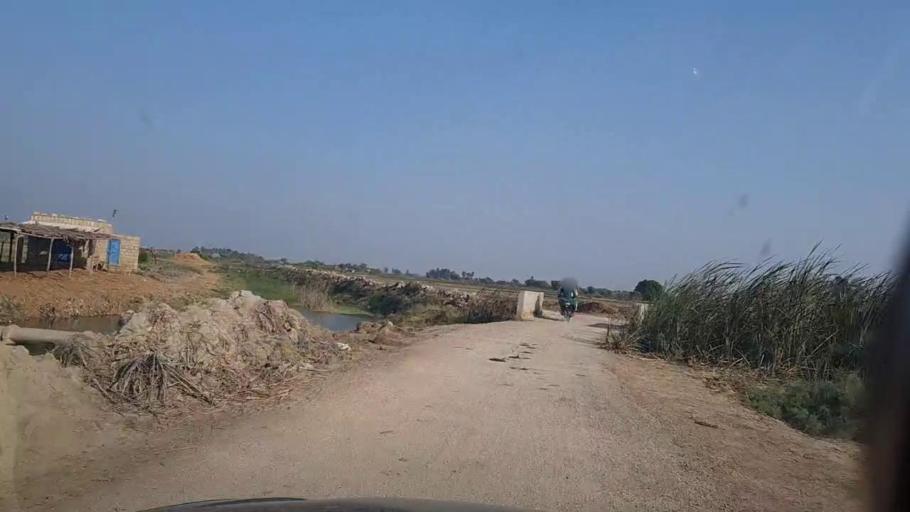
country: PK
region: Sindh
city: Thatta
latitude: 24.5859
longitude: 67.8789
